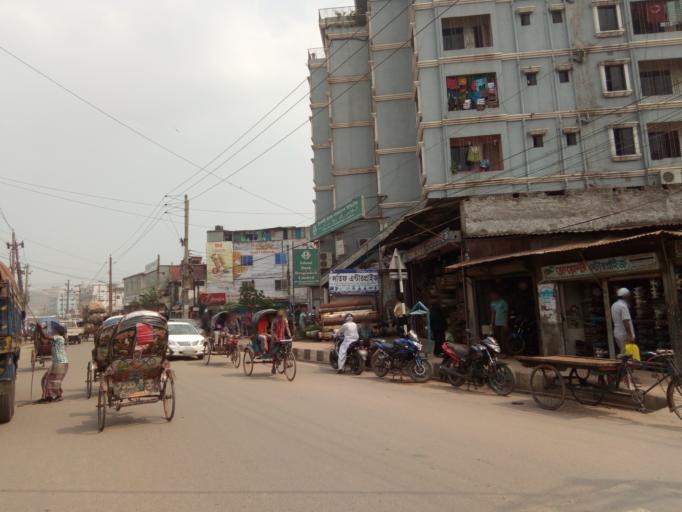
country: BD
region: Dhaka
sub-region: Dhaka
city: Dhaka
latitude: 23.6927
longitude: 90.4289
